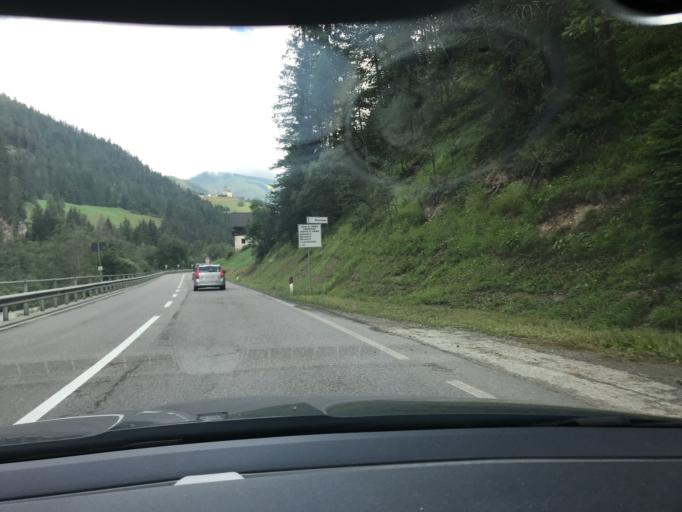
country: IT
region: Trentino-Alto Adige
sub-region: Bolzano
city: San Martino in Badia
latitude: 46.6714
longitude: 11.9040
